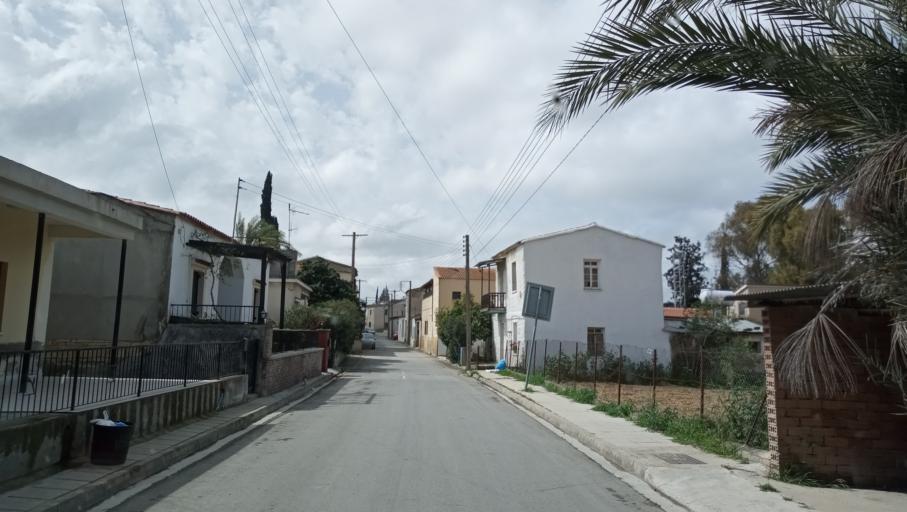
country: CY
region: Lefkosia
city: Dali
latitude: 35.0276
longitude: 33.4247
